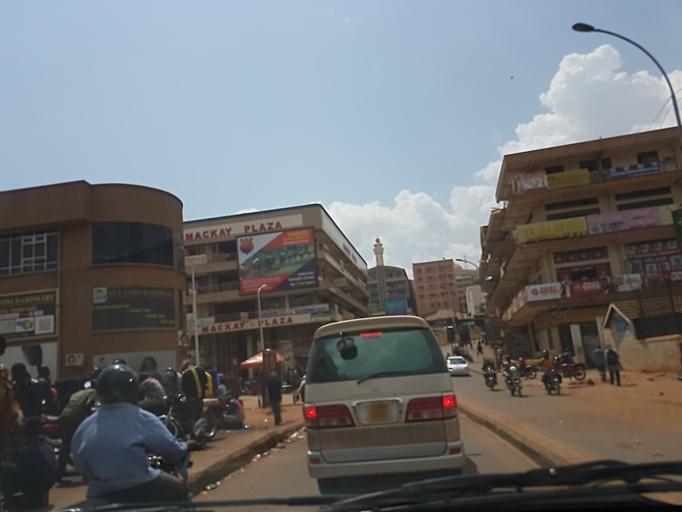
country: UG
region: Central Region
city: Kampala Central Division
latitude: 0.3170
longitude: 32.5722
